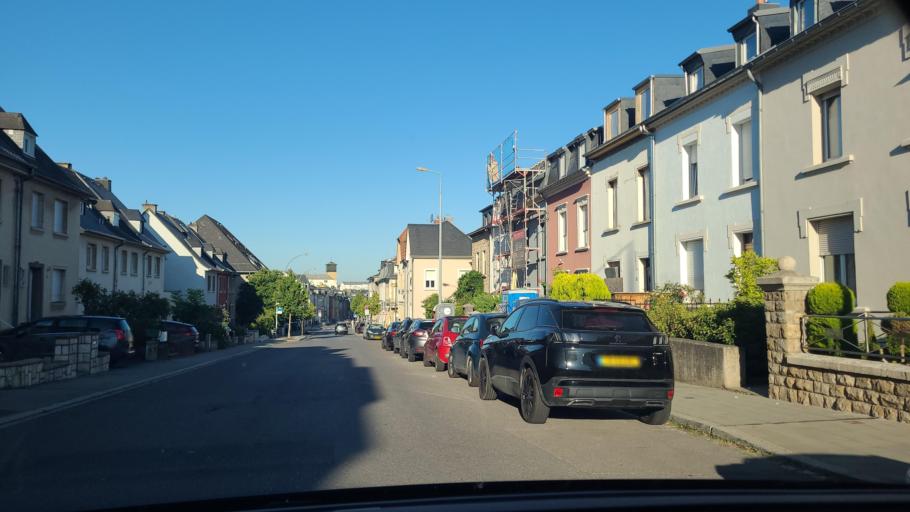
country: LU
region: Luxembourg
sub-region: Canton de Luxembourg
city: Luxembourg
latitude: 49.5982
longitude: 6.1459
